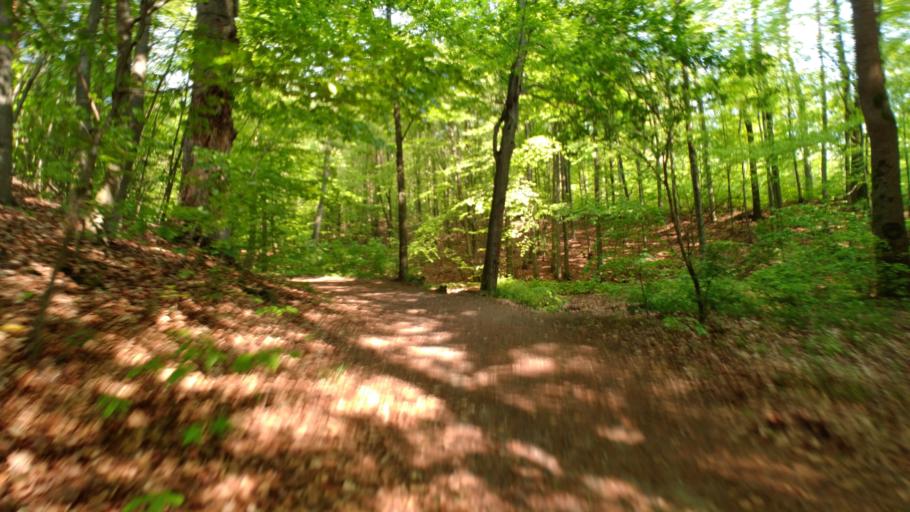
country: DE
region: Saxony
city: Albertstadt
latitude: 51.0755
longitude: 13.7996
